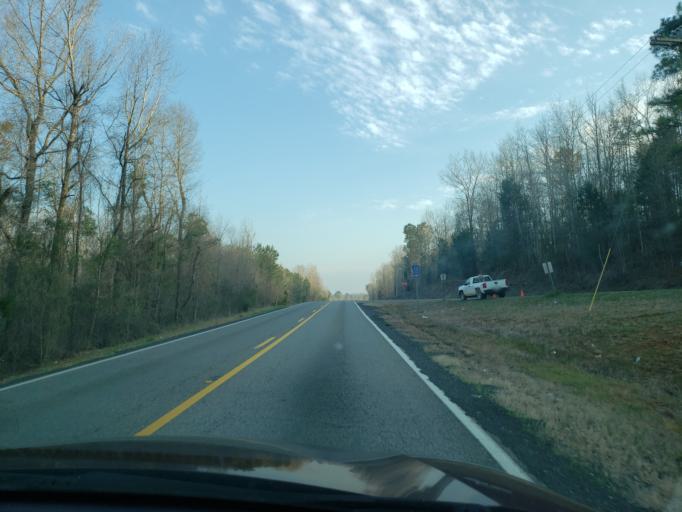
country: US
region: Alabama
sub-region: Hale County
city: Greensboro
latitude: 32.7799
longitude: -87.5875
